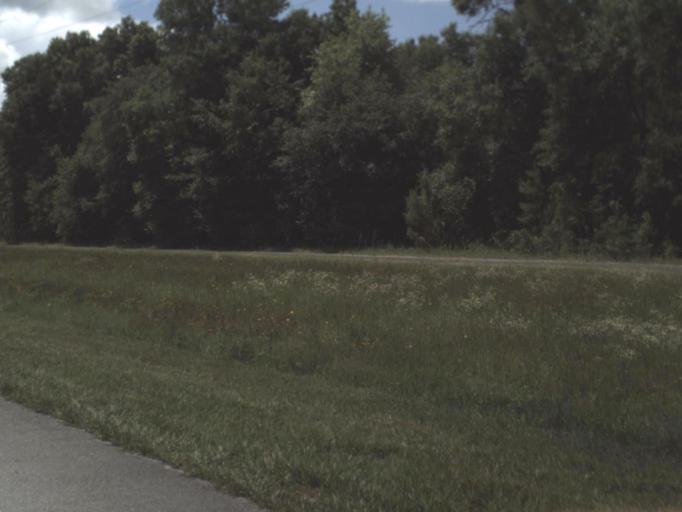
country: US
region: Florida
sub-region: Putnam County
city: Palatka
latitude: 29.5176
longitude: -81.6188
